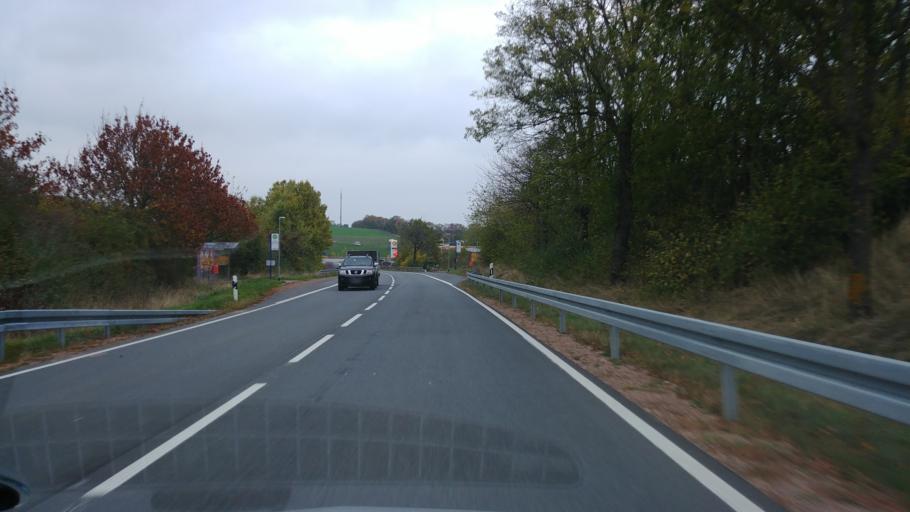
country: DE
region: Hesse
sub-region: Regierungsbezirk Darmstadt
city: Idstein
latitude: 50.2243
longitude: 8.2002
